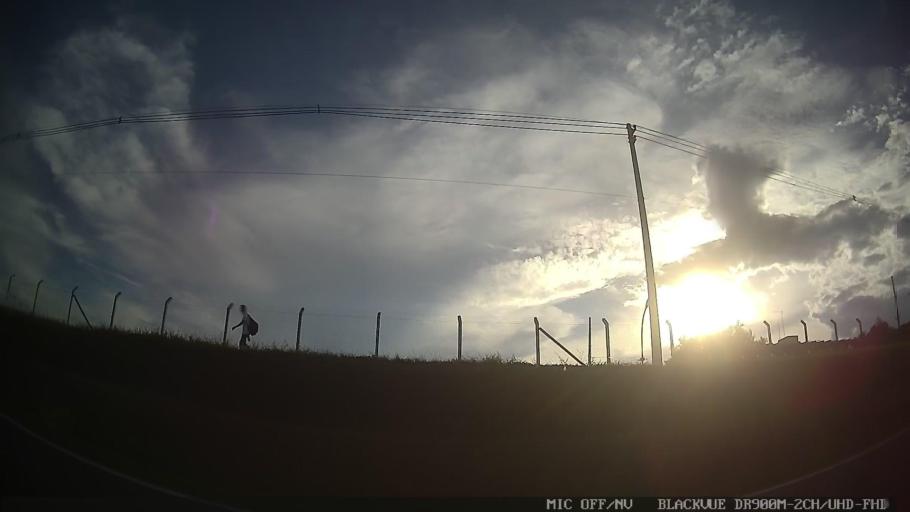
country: BR
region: Sao Paulo
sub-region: Tiete
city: Tiete
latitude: -23.1121
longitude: -47.7229
